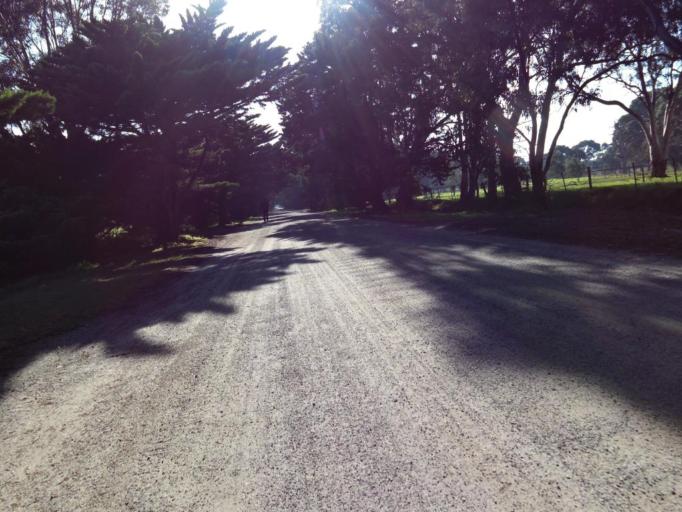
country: AU
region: Victoria
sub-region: Kingston
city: Dingley Village
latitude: -37.9967
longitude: 145.1246
